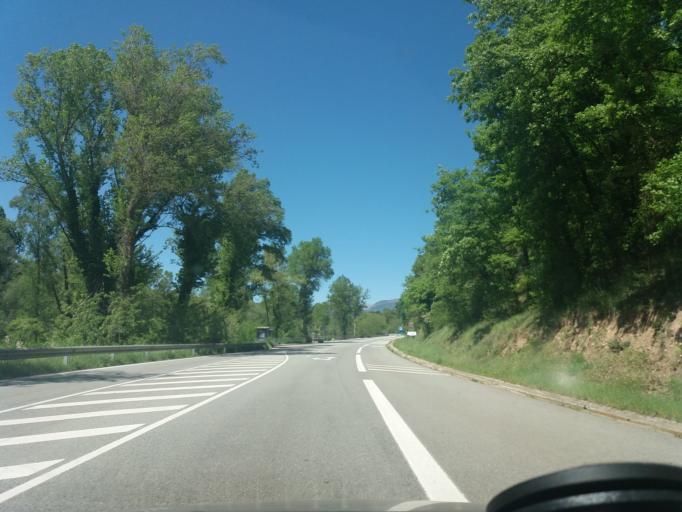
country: ES
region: Catalonia
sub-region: Provincia de Barcelona
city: Gironella
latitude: 42.0512
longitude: 1.8729
